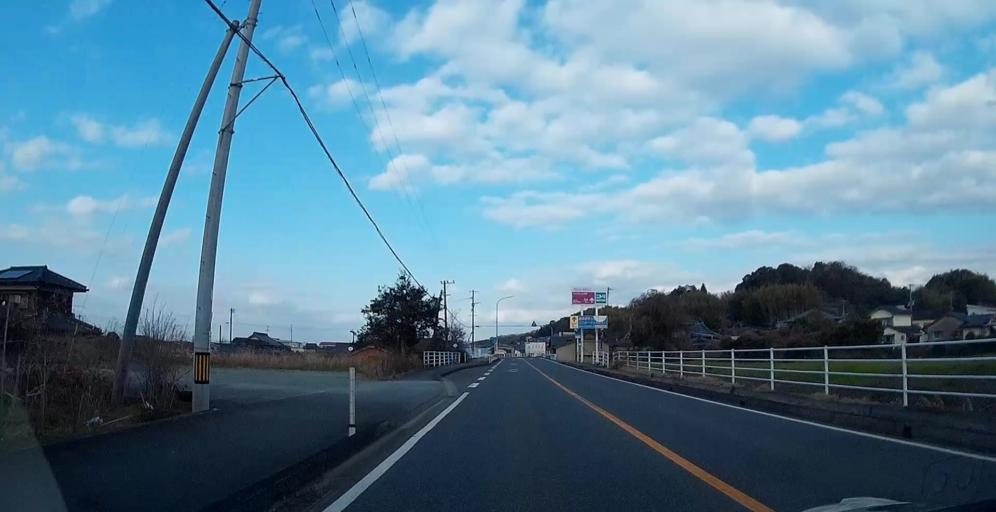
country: JP
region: Kumamoto
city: Yatsushiro
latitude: 32.5453
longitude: 130.6765
